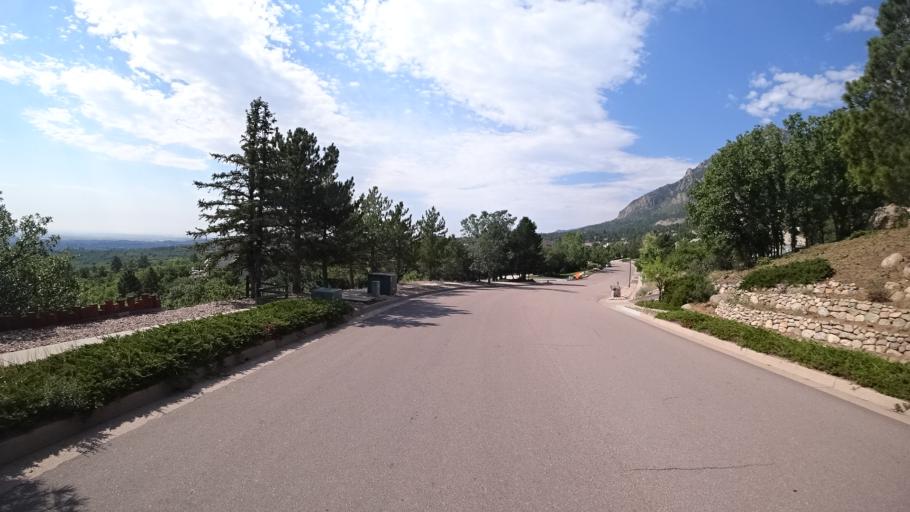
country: US
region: Colorado
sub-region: El Paso County
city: Fort Carson
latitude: 38.7553
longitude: -104.8320
